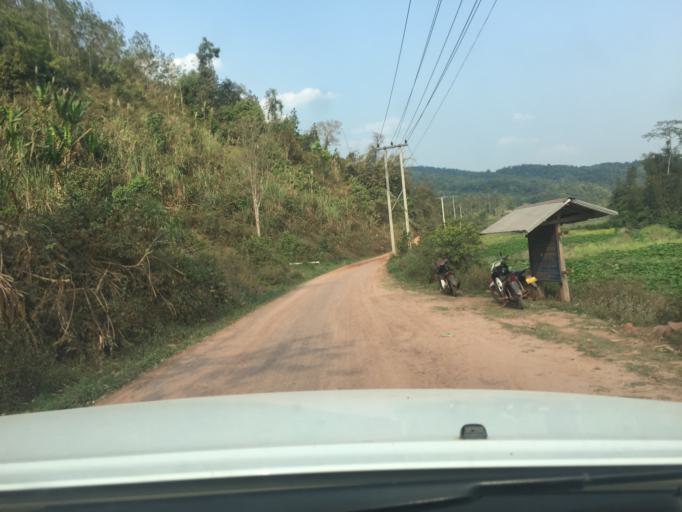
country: LA
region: Oudomxai
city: Muang La
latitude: 21.0744
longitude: 101.8253
